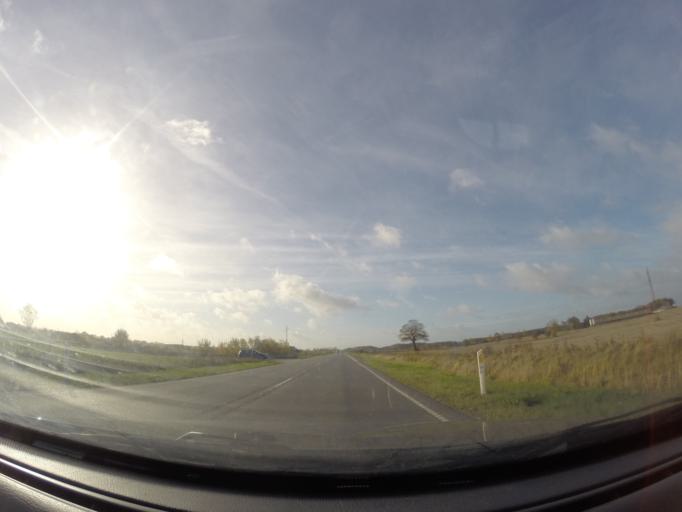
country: DK
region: South Denmark
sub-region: Faaborg-Midtfyn Kommune
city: Ringe
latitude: 55.1933
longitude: 10.5330
